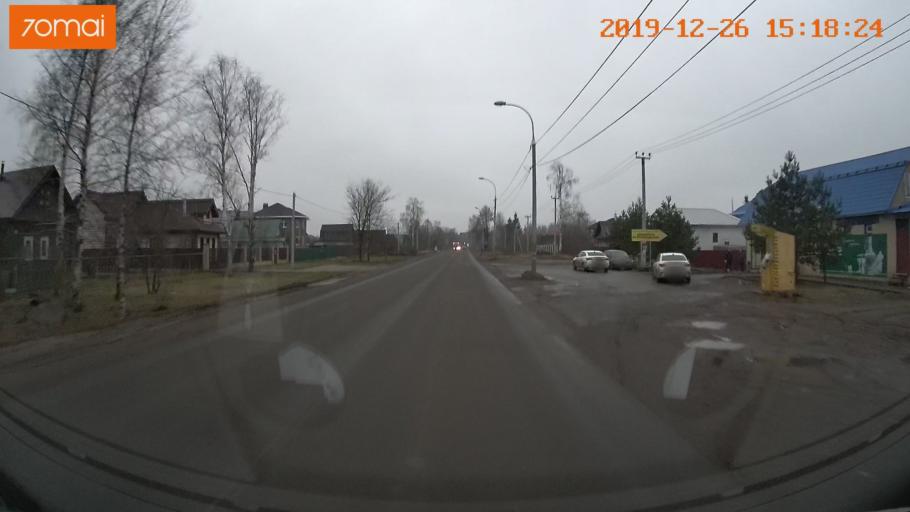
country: RU
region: Jaroslavl
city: Rybinsk
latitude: 58.0698
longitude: 38.8442
